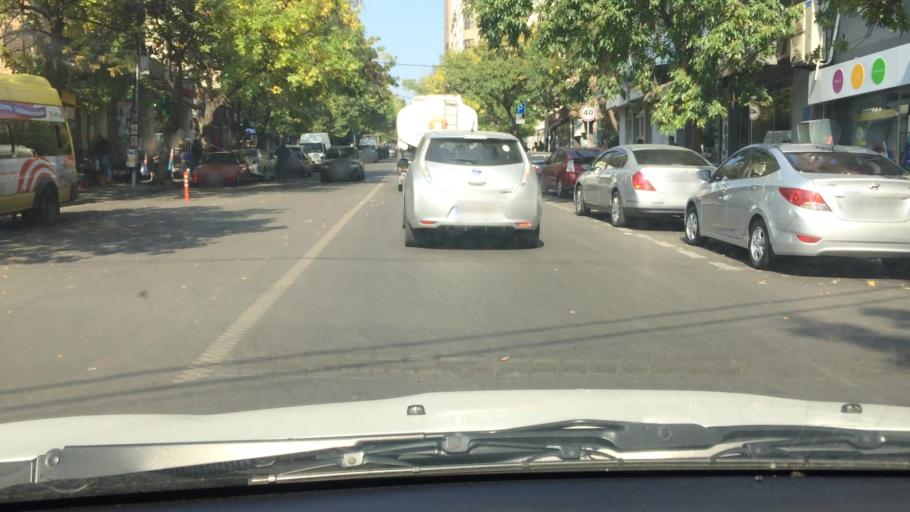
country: GE
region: T'bilisi
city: Tbilisi
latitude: 41.6882
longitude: 44.8276
